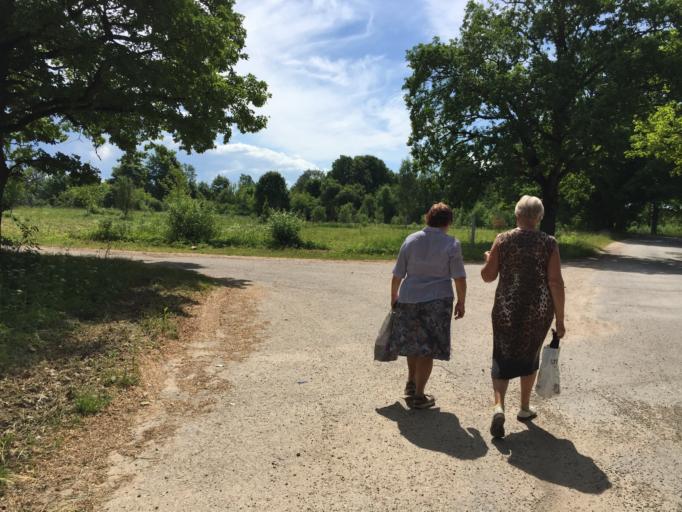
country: LV
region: Pargaujas
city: Stalbe
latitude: 57.3534
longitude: 24.9481
